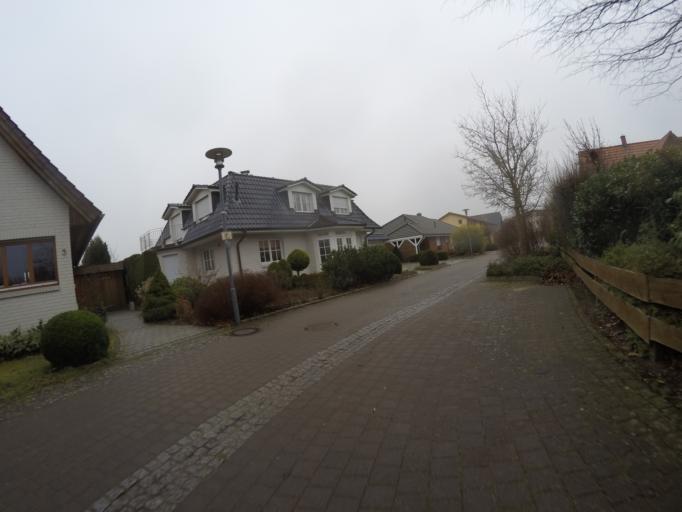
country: DE
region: Schleswig-Holstein
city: Quickborn
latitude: 53.7318
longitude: 9.8880
